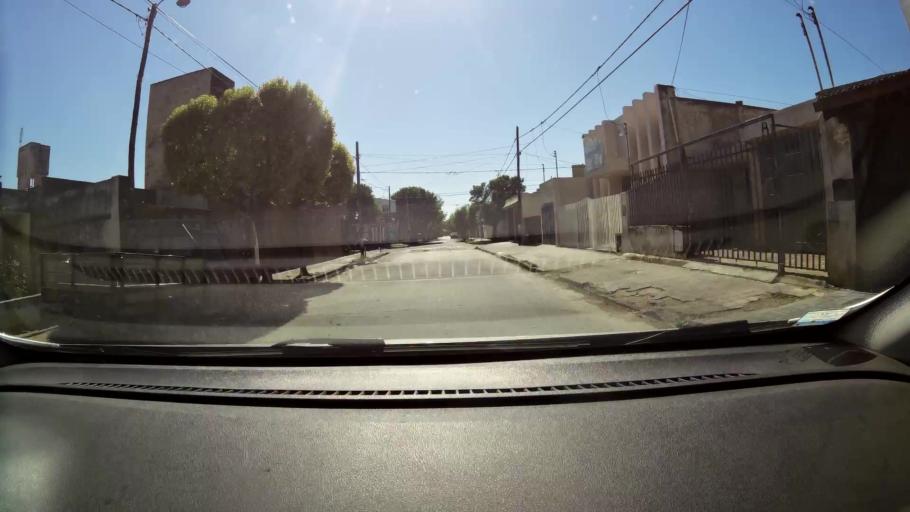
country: AR
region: Cordoba
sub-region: Departamento de Capital
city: Cordoba
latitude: -31.4398
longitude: -64.1517
